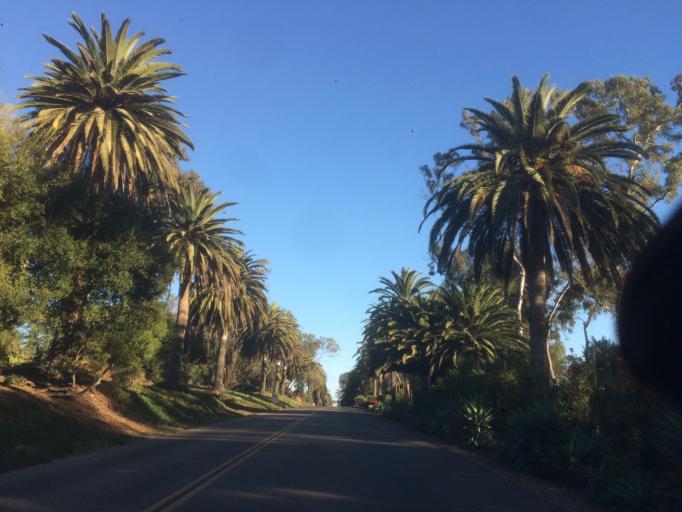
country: US
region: California
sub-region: Santa Barbara County
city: Mission Canyon
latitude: 34.4113
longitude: -119.7633
